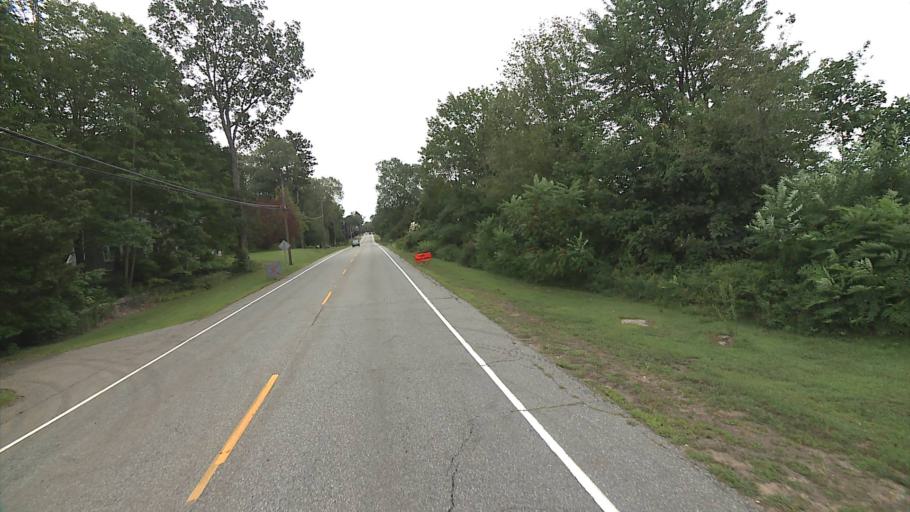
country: US
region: Connecticut
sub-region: Hartford County
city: Manchester
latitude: 41.7539
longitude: -72.4396
